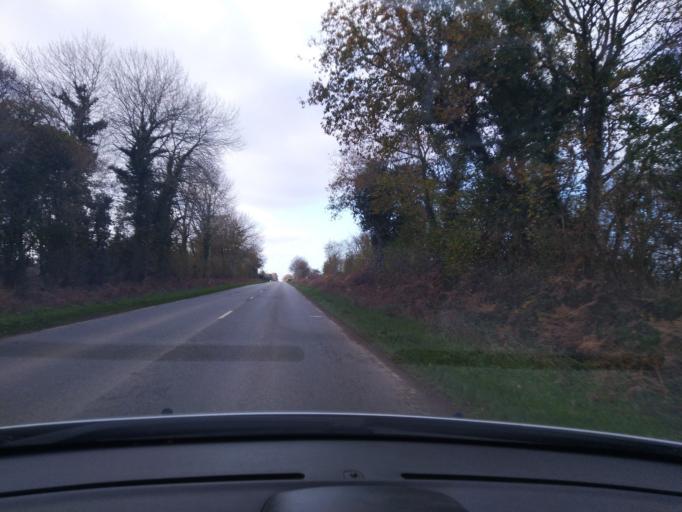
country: FR
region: Brittany
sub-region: Departement du Finistere
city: Plouigneau
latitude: 48.5738
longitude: -3.7470
